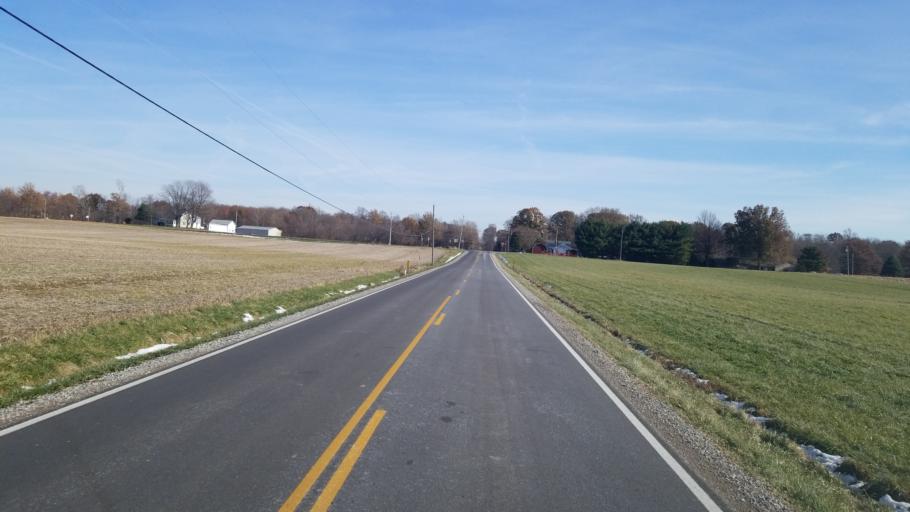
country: US
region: Ohio
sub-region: Huron County
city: Norwalk
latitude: 41.1917
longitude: -82.6292
